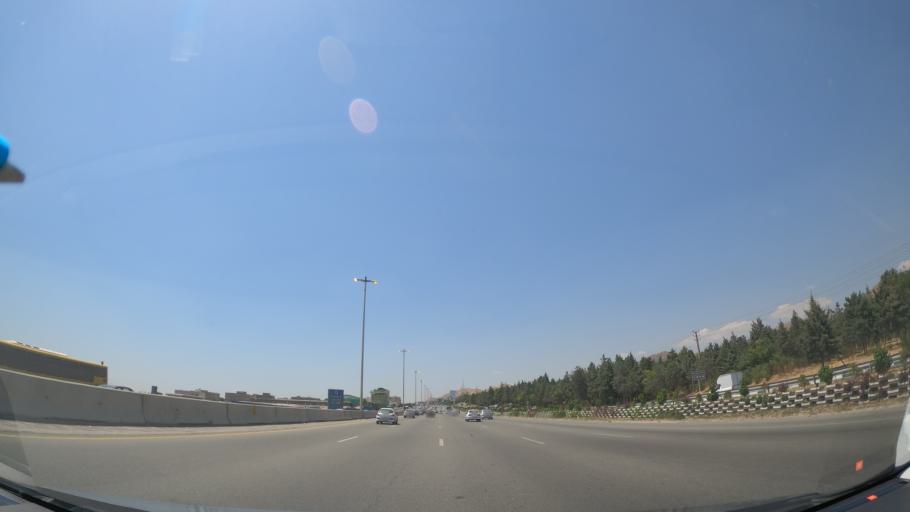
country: IR
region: Alborz
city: Karaj
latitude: 35.7768
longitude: 51.0377
